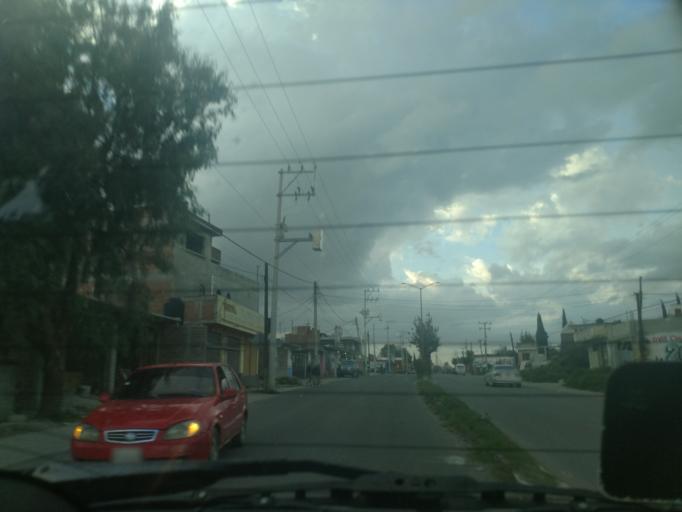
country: MX
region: Morelos
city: Coyotepec
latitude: 19.7631
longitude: -99.2011
